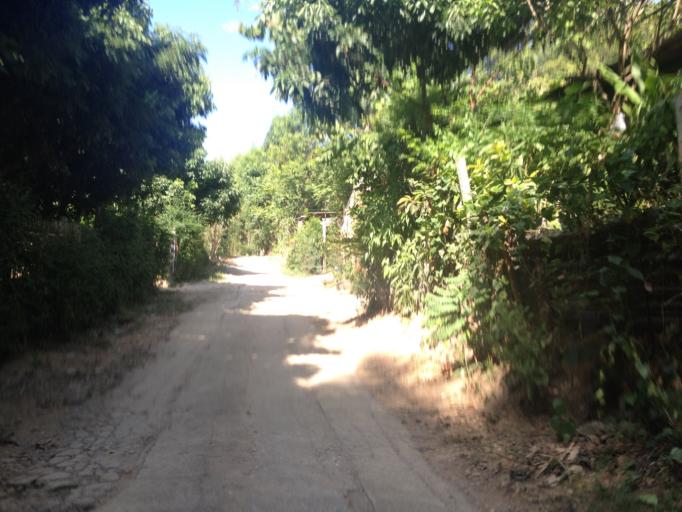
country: TH
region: Chiang Mai
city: Hang Dong
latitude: 18.7353
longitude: 98.9071
